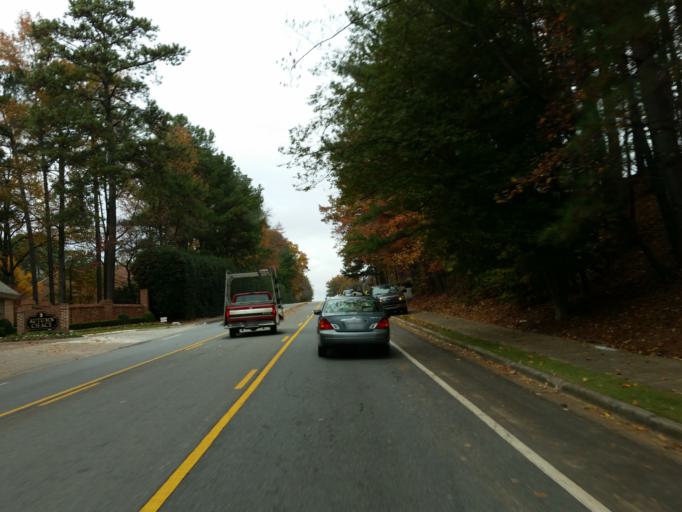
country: US
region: Georgia
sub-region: Fulton County
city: Sandy Springs
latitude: 33.9247
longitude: -84.3599
